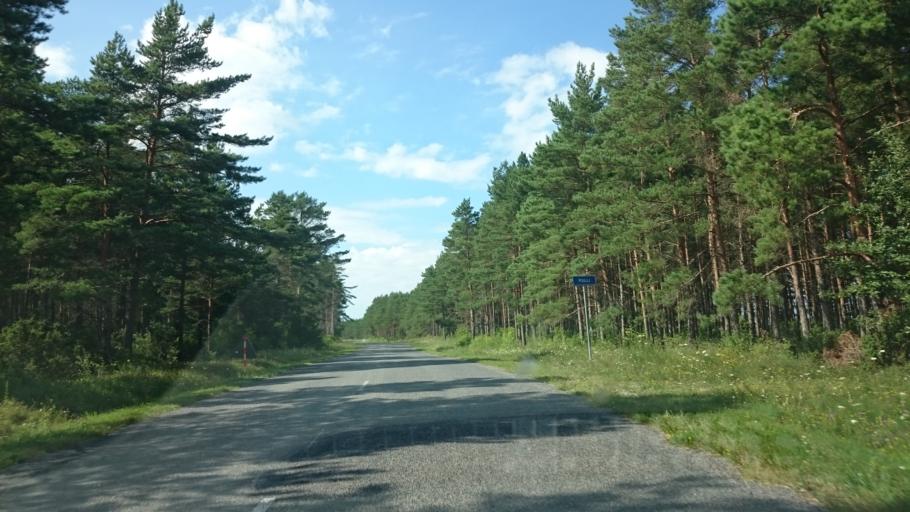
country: EE
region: Saare
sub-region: Orissaare vald
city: Orissaare
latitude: 58.5877
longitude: 23.0208
